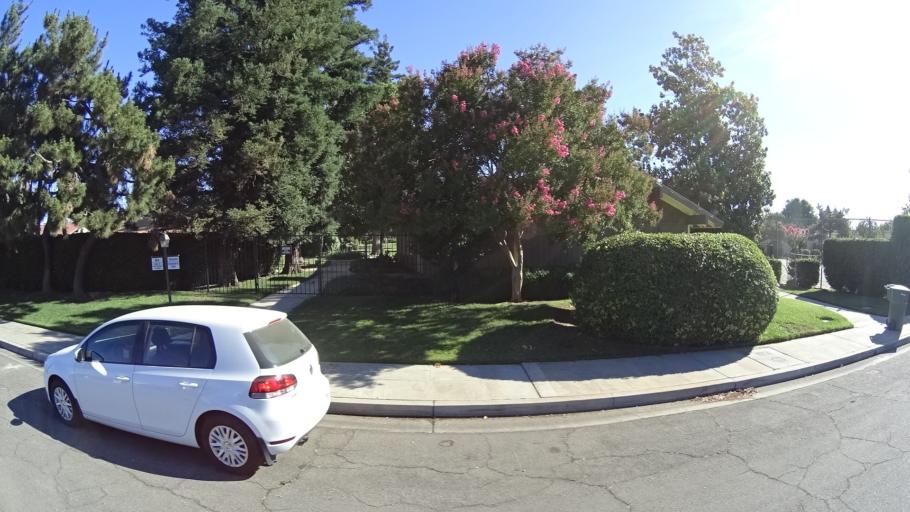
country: US
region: California
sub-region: Fresno County
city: Fresno
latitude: 36.8045
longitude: -119.8328
